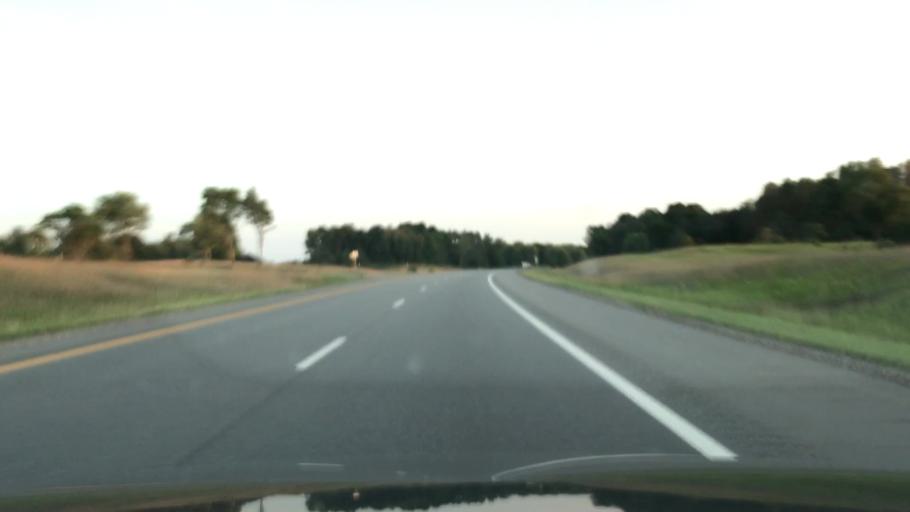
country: US
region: Michigan
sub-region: Montcalm County
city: Howard City
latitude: 43.4675
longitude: -85.4770
